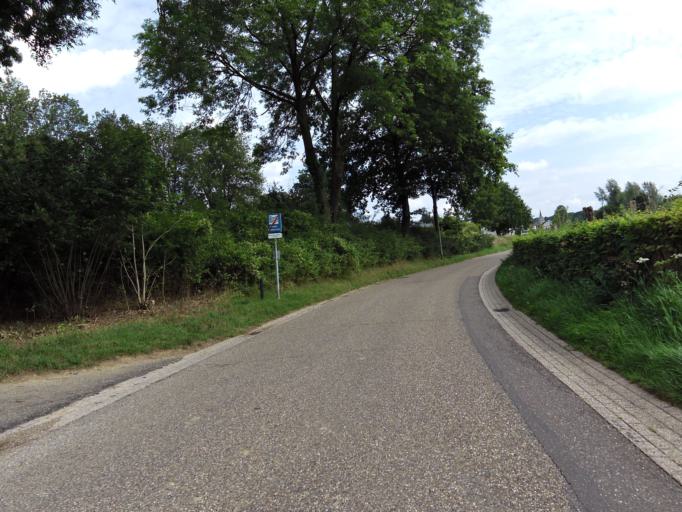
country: NL
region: Limburg
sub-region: Gemeente Simpelveld
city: Simpelveld
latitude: 50.8363
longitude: 5.9699
